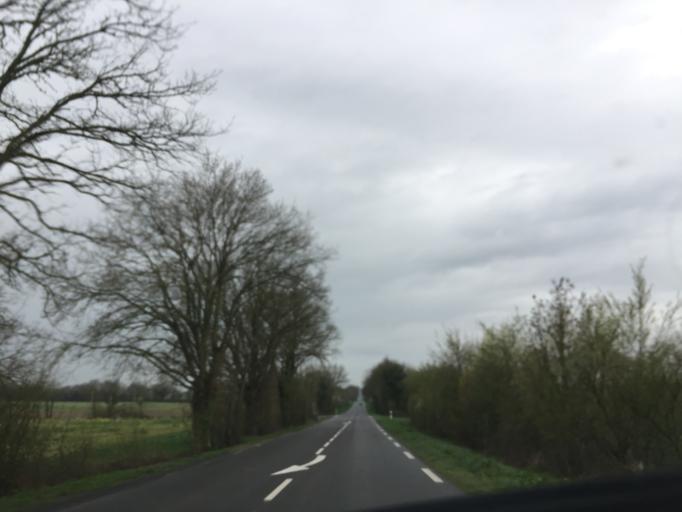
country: FR
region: Pays de la Loire
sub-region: Departement de la Loire-Atlantique
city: Moisdon-la-Riviere
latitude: 47.6123
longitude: -1.3787
